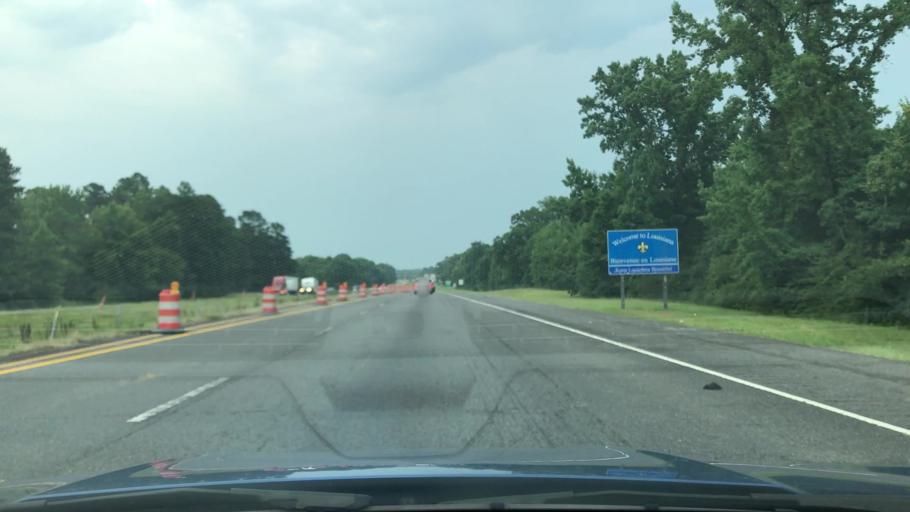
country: US
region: Texas
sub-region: Harrison County
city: Waskom
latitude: 32.4603
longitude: -94.0413
